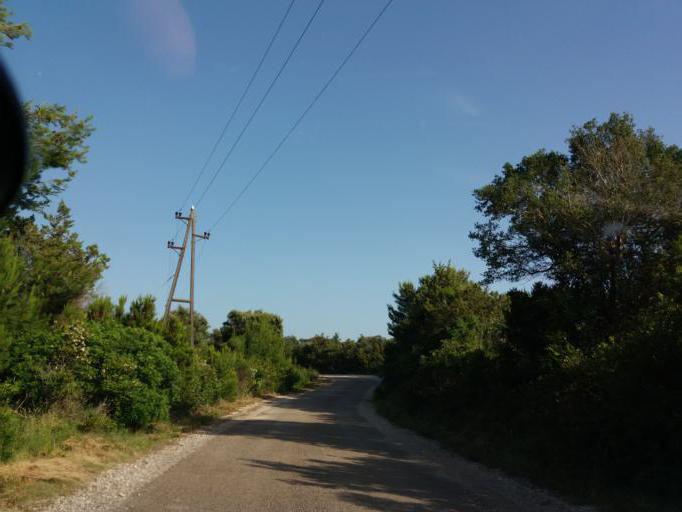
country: HR
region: Zadarska
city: Ugljan
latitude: 44.1495
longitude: 14.8256
